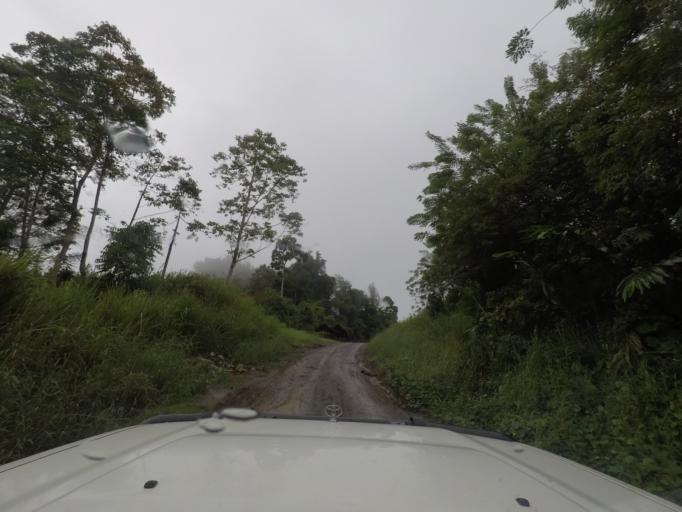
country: PG
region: Madang
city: Madang
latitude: -5.4781
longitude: 145.4849
